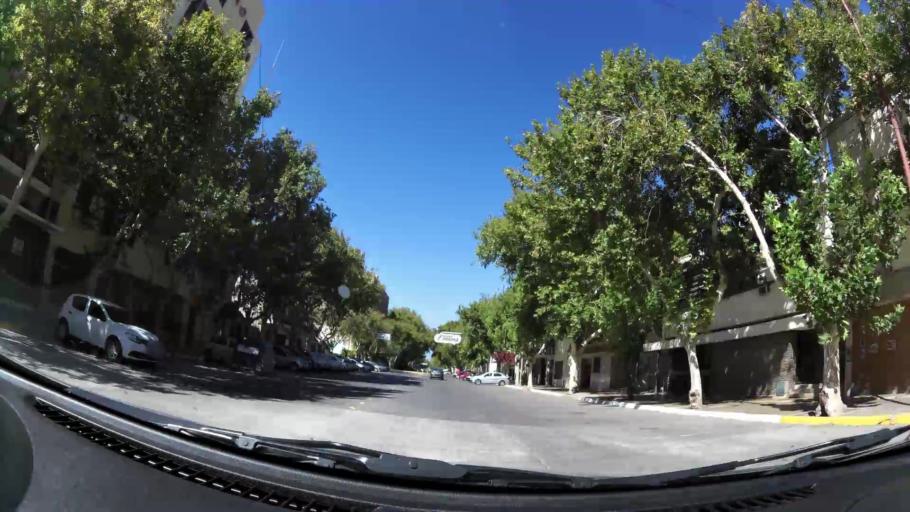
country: AR
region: San Juan
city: San Juan
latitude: -31.5378
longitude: -68.5329
